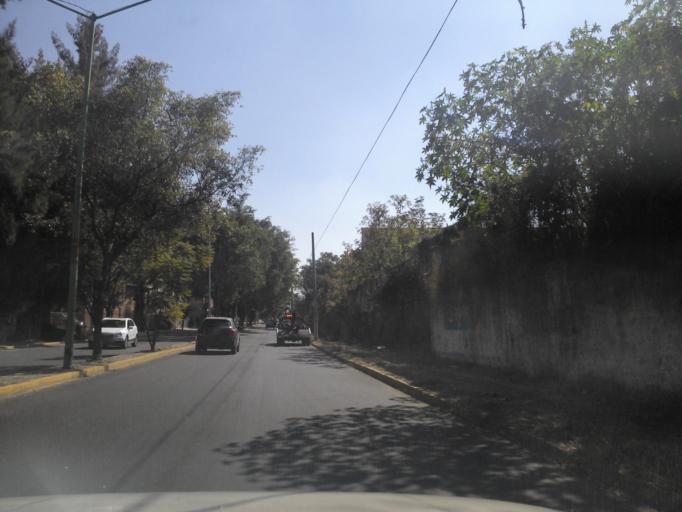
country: MX
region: Jalisco
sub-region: Zapopan
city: Zapopan
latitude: 20.7036
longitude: -103.3584
